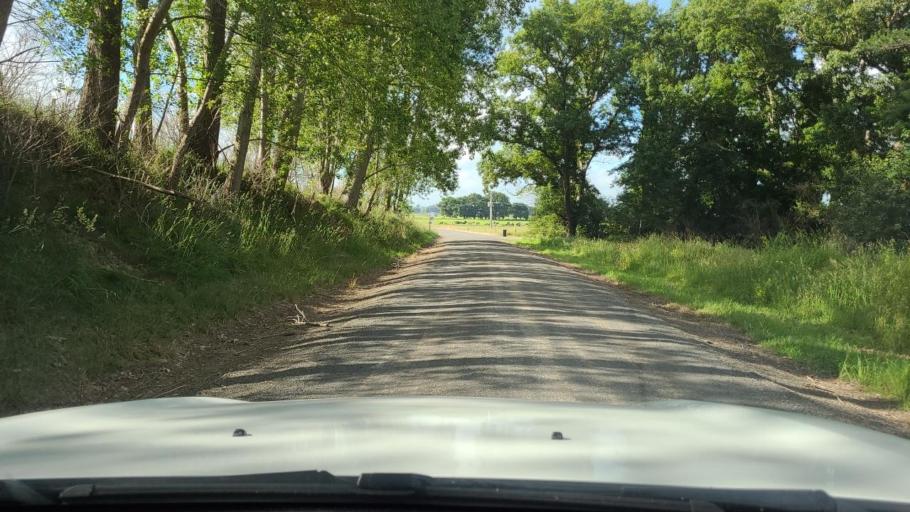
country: NZ
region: Bay of Plenty
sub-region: Western Bay of Plenty District
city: Katikati
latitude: -37.6125
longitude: 175.7957
